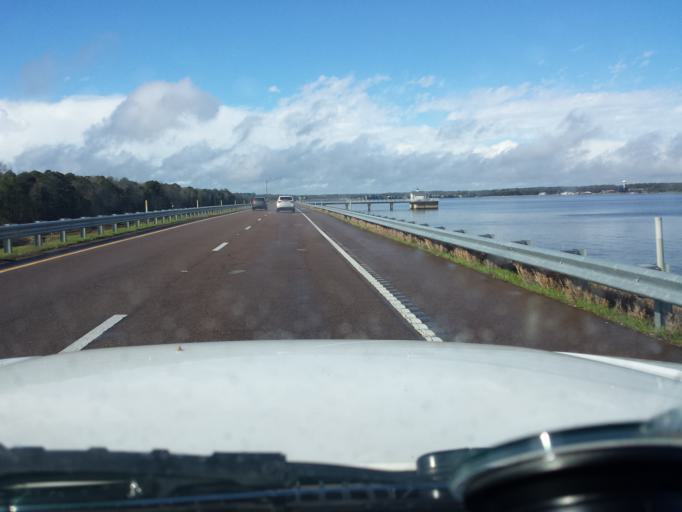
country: US
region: Mississippi
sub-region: Madison County
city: Ridgeland
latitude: 32.4024
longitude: -90.0722
